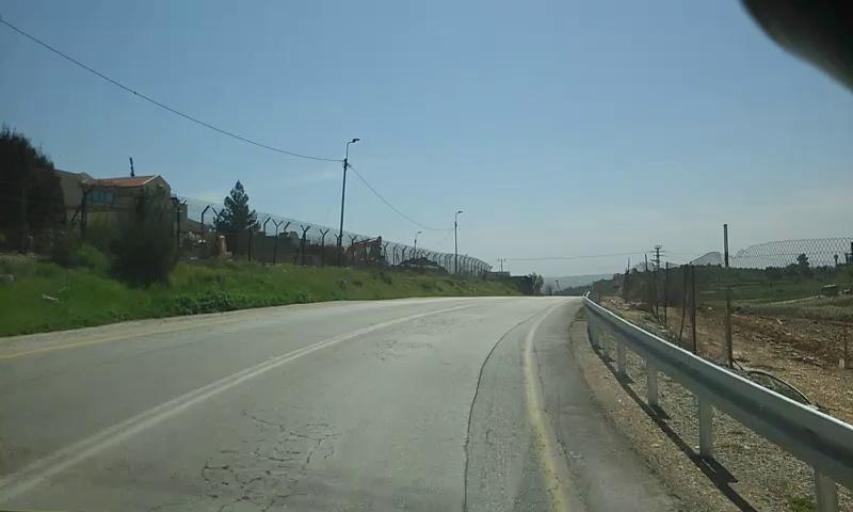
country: PS
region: West Bank
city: Nahhalin
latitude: 31.6528
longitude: 35.1254
